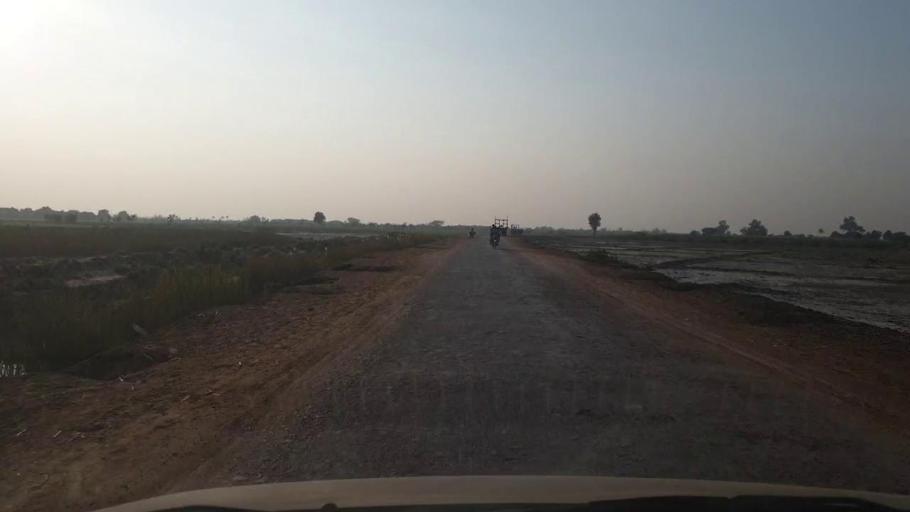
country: PK
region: Sindh
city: Mirwah Gorchani
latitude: 25.3683
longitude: 69.1345
